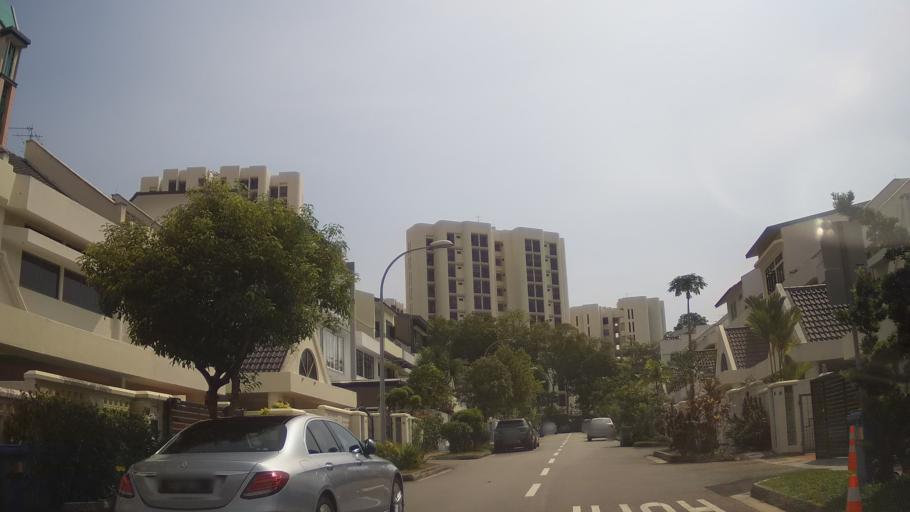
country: MY
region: Johor
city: Johor Bahru
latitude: 1.3722
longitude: 103.7655
